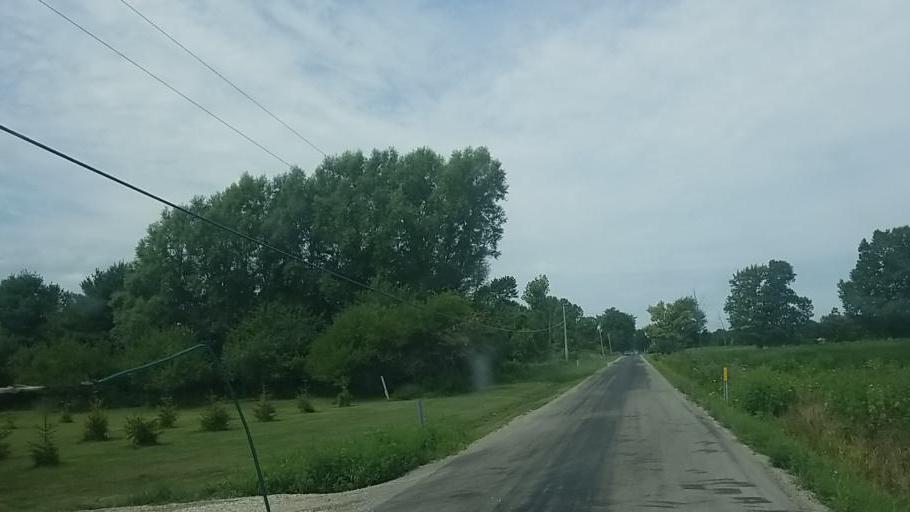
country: US
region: Ohio
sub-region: Delaware County
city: Sunbury
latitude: 40.2025
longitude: -82.7918
